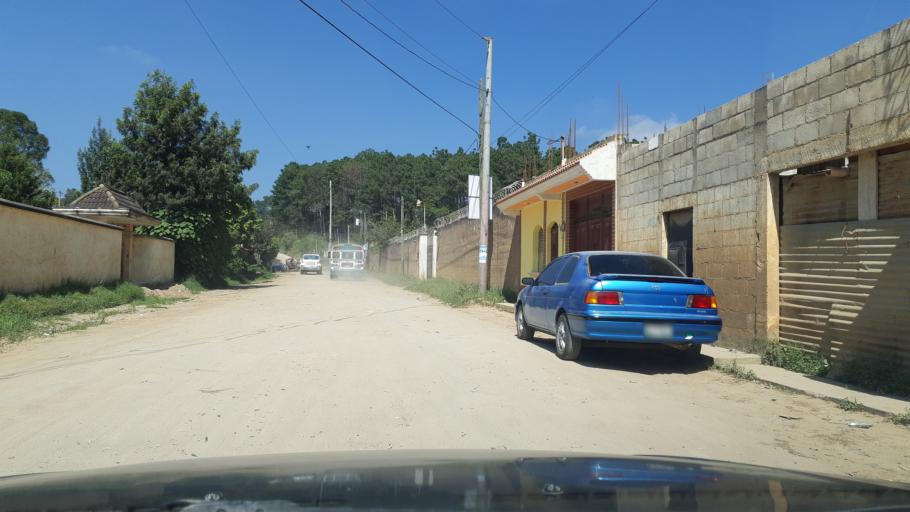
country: GT
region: Chimaltenango
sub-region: Municipio de Chimaltenango
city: Chimaltenango
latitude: 14.6697
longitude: -90.8376
